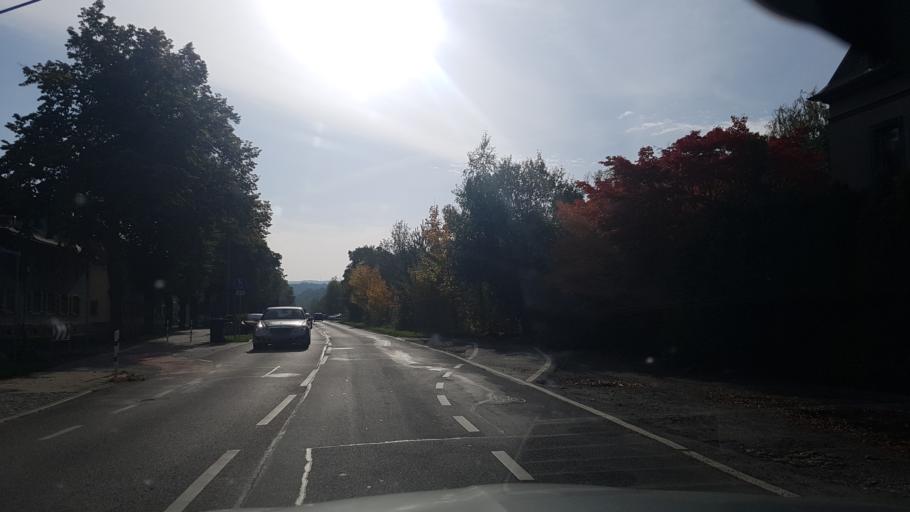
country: DE
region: Saxony
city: Pirna
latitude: 50.9385
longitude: 13.9449
